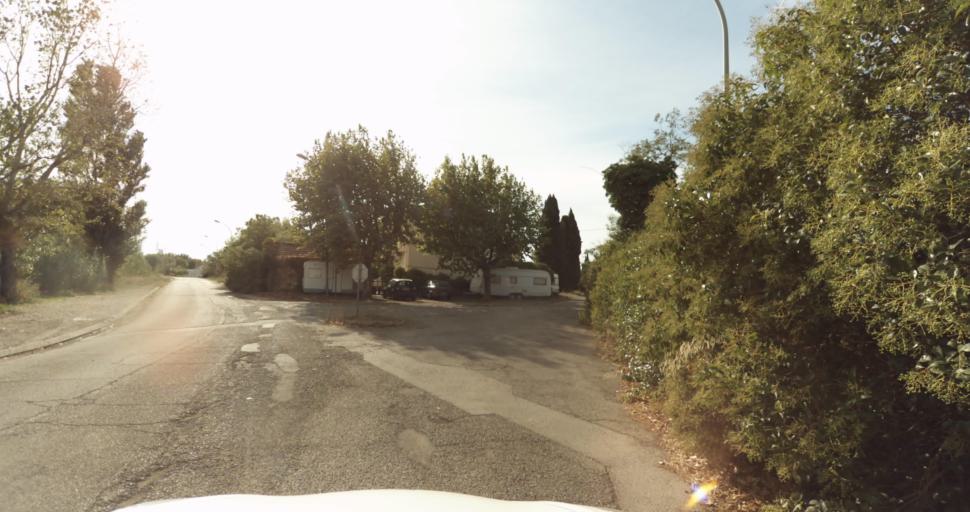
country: FR
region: Provence-Alpes-Cote d'Azur
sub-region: Departement des Bouches-du-Rhone
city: Miramas
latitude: 43.5793
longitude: 4.9928
